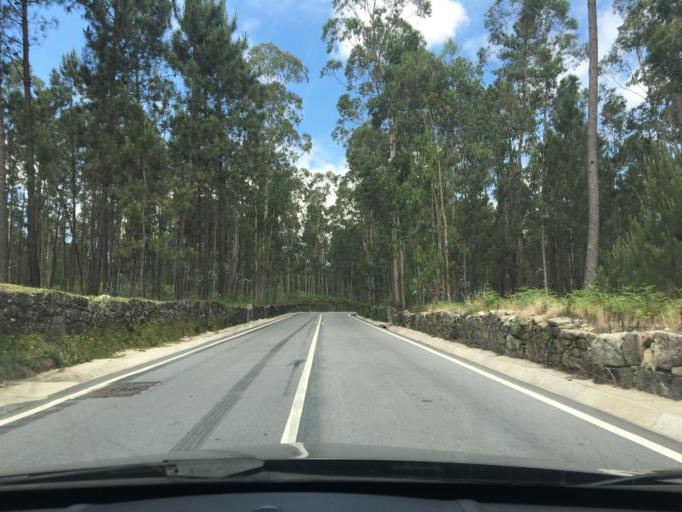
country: PT
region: Porto
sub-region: Maia
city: Anta
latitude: 41.2885
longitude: -8.6063
